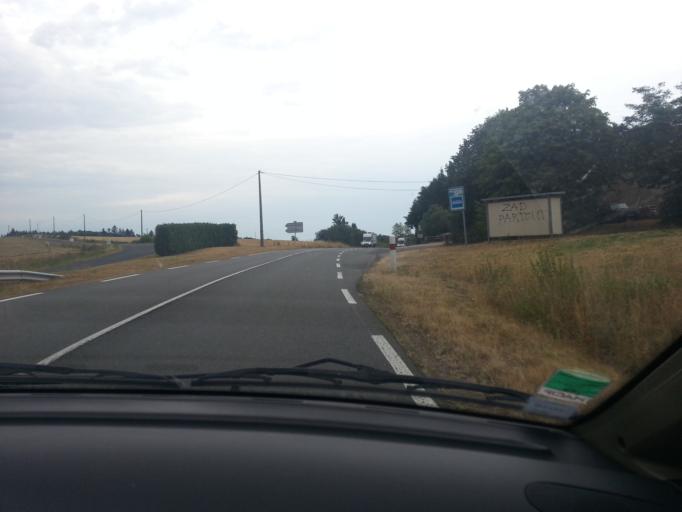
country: FR
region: Auvergne
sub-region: Departement de l'Allier
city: Le Donjon
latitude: 46.2944
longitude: 3.7518
